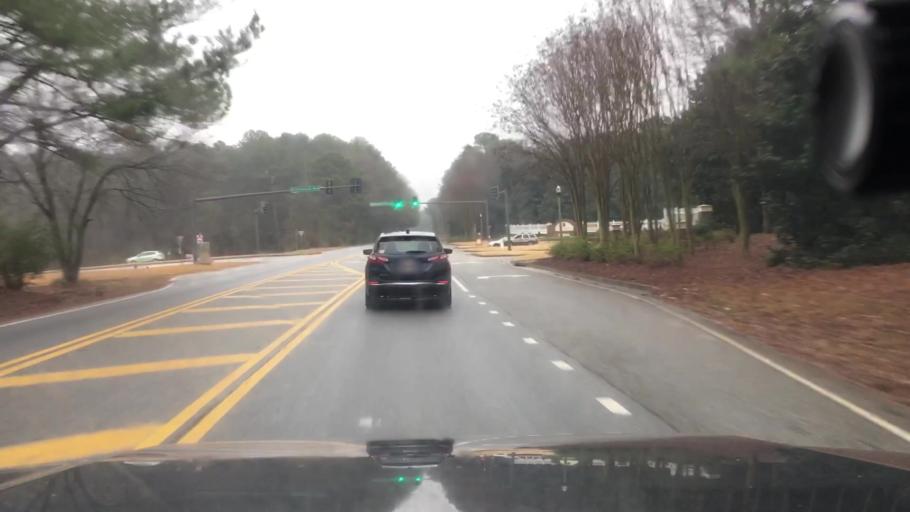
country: US
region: Georgia
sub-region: Coweta County
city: East Newnan
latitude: 33.3803
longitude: -84.7391
